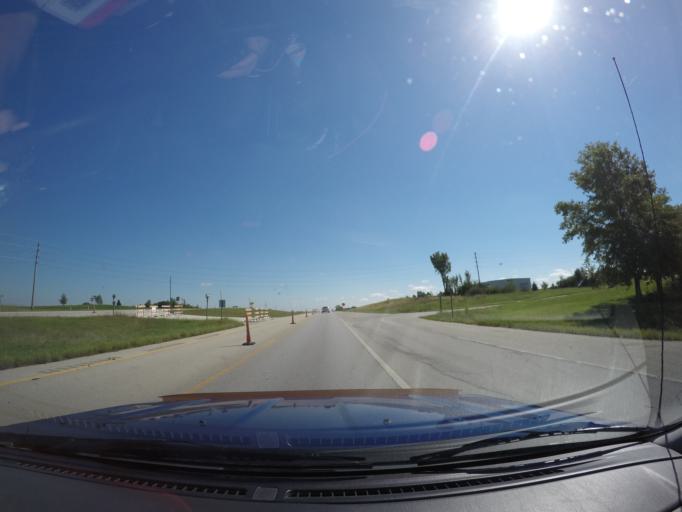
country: US
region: Kansas
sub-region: Douglas County
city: Lawrence
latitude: 38.9423
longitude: -95.1960
